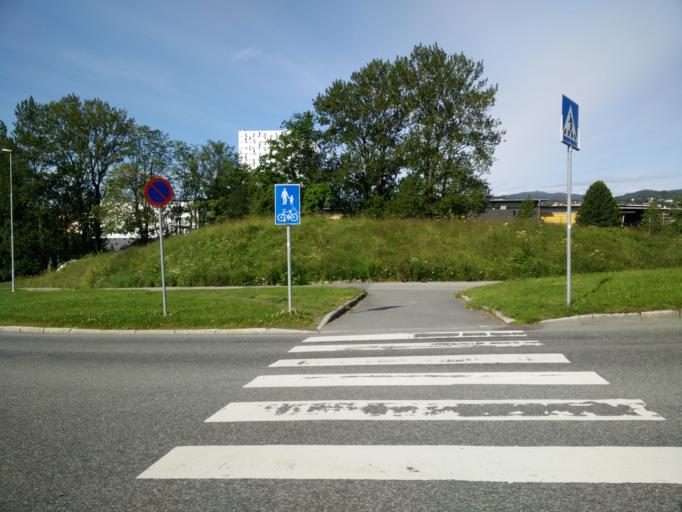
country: NO
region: Sor-Trondelag
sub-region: Trondheim
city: Trondheim
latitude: 63.4125
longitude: 10.4088
